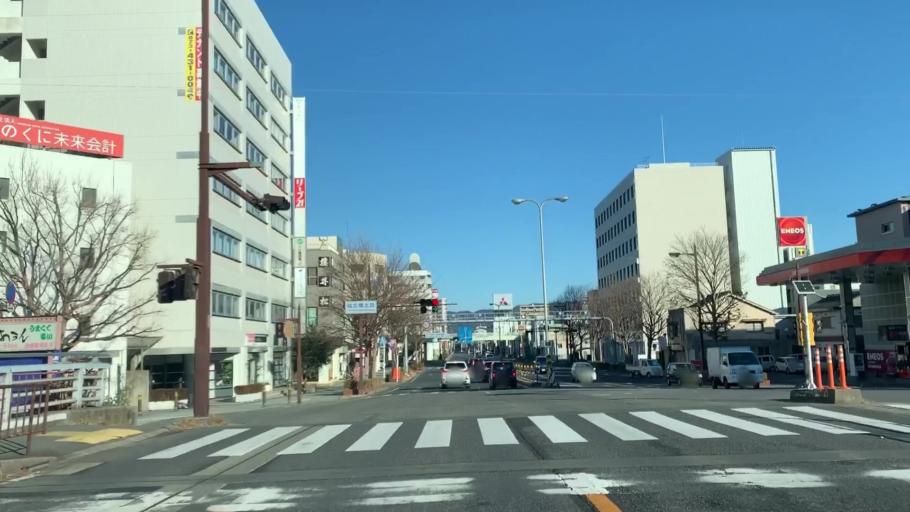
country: JP
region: Wakayama
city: Wakayama-shi
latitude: 34.2325
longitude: 135.1695
